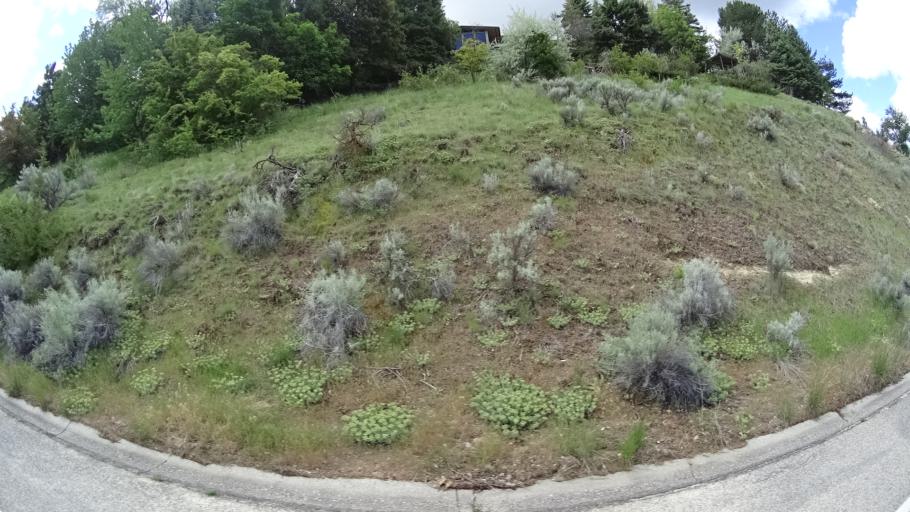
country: US
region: Idaho
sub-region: Ada County
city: Boise
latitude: 43.6477
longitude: -116.1907
